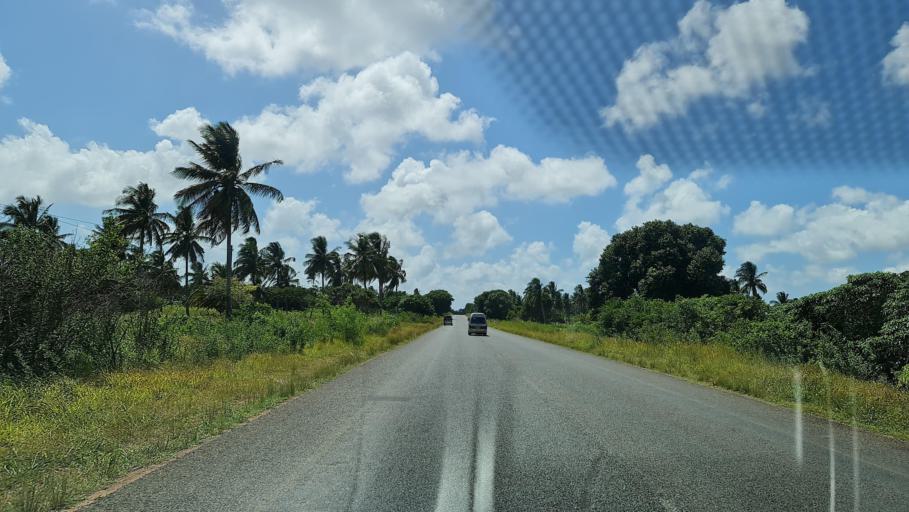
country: MZ
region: Inhambane
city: Maxixe
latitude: -24.5409
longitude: 34.9196
